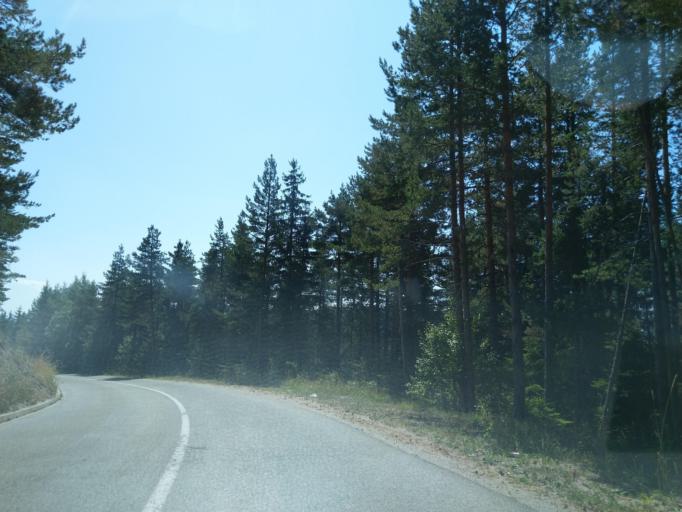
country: RS
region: Central Serbia
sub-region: Zlatiborski Okrug
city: Nova Varos
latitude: 43.3634
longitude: 19.8518
